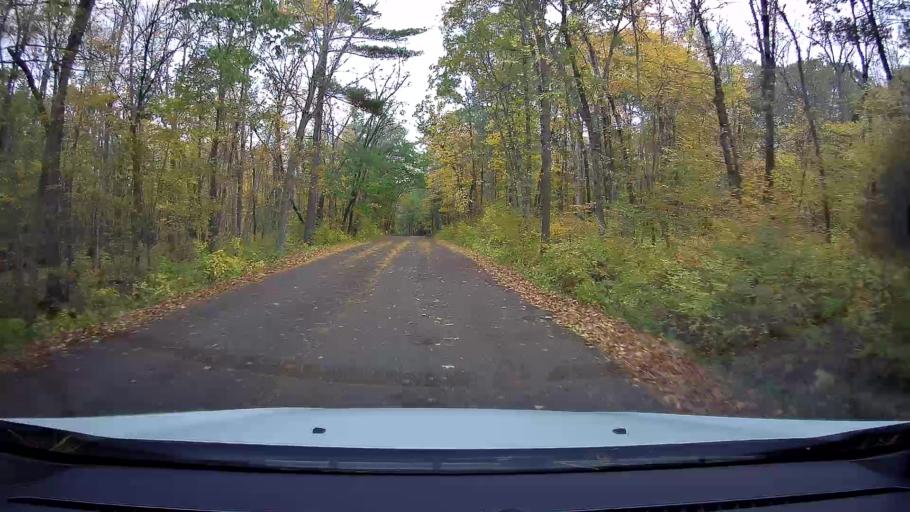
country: US
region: Wisconsin
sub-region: Polk County
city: Saint Croix Falls
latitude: 45.3909
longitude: -92.6523
